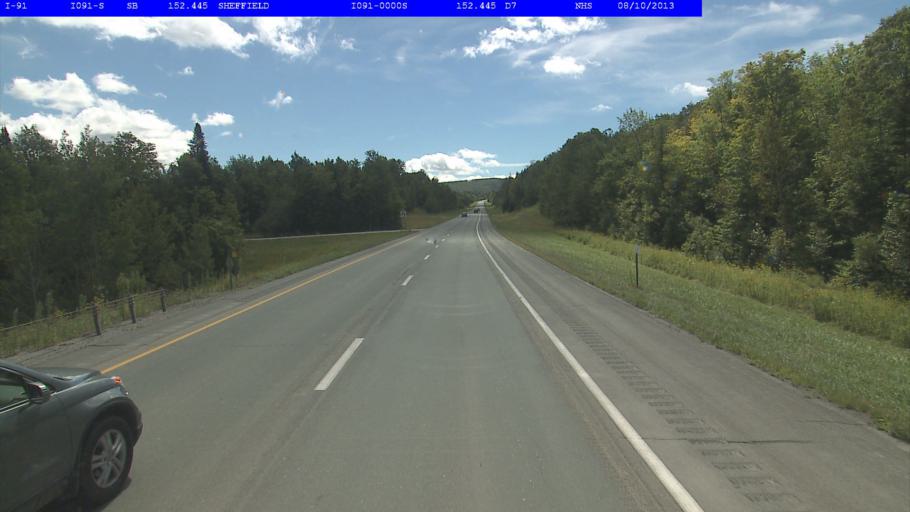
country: US
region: Vermont
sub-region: Caledonia County
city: Lyndonville
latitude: 44.6984
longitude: -72.1440
